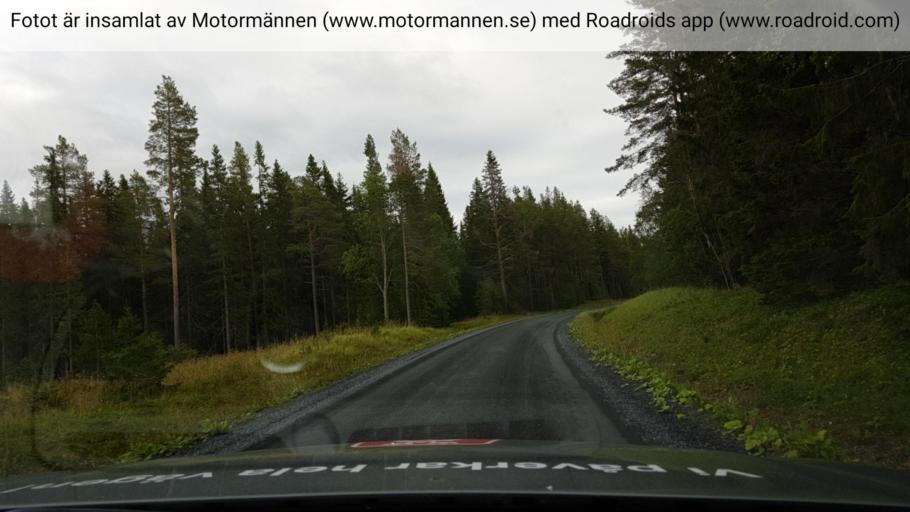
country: SE
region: Jaemtland
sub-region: Krokoms Kommun
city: Valla
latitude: 63.3662
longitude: 13.9525
